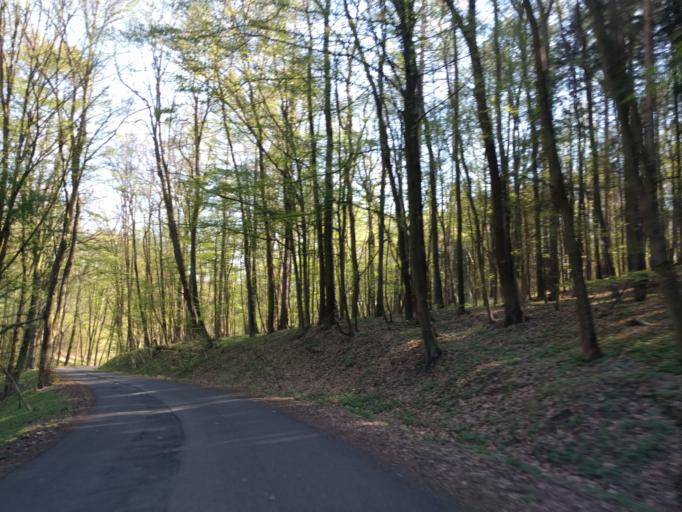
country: CZ
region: Central Bohemia
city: Kostelec nad Cernymi Lesy
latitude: 50.0244
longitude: 14.8112
